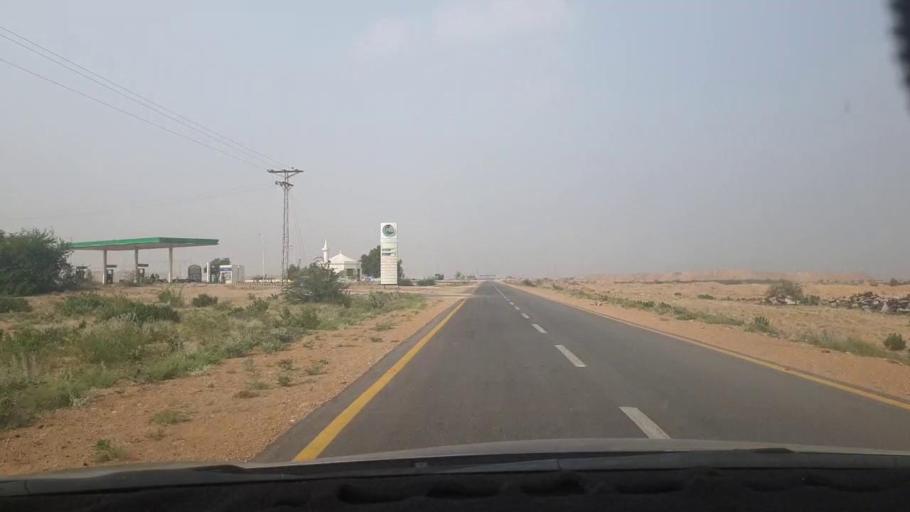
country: PK
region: Sindh
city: Matiari
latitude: 25.5706
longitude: 68.3156
